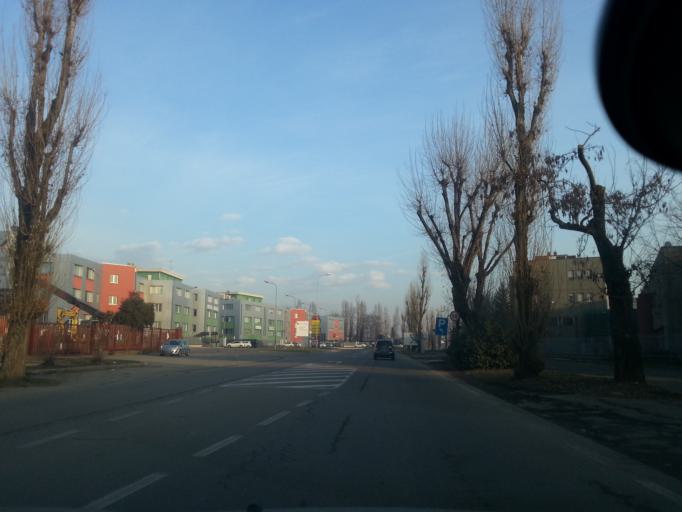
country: IT
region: Lombardy
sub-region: Citta metropolitana di Milano
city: Pero
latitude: 45.5284
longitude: 9.0848
